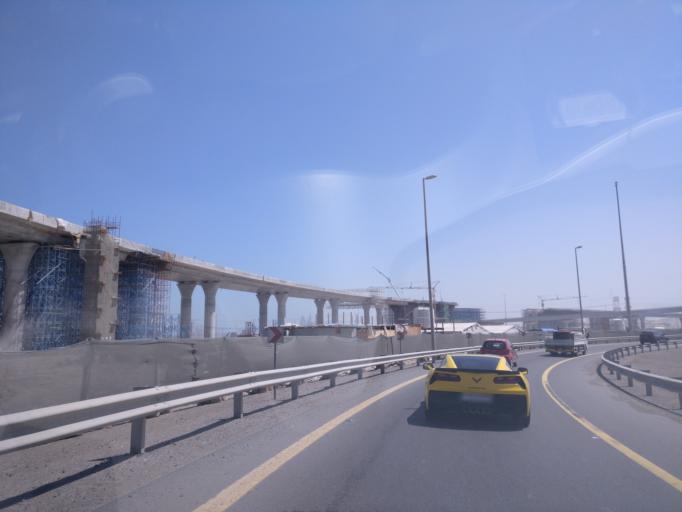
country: AE
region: Dubai
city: Dubai
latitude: 25.0173
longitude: 55.0961
